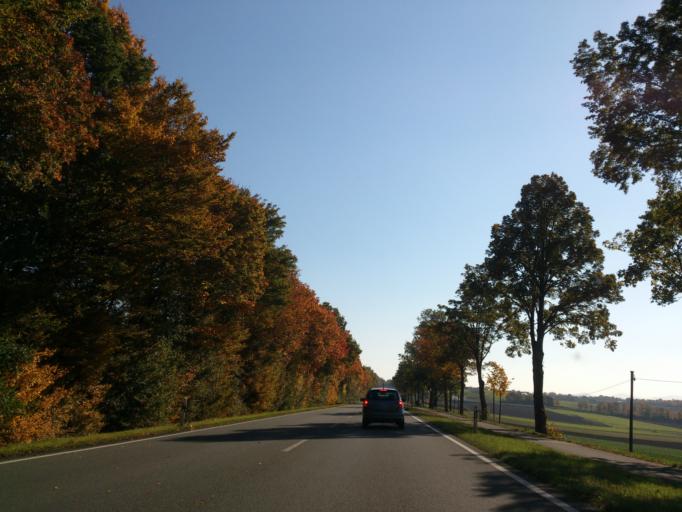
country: DE
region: North Rhine-Westphalia
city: Warburg
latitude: 51.5006
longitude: 9.1110
